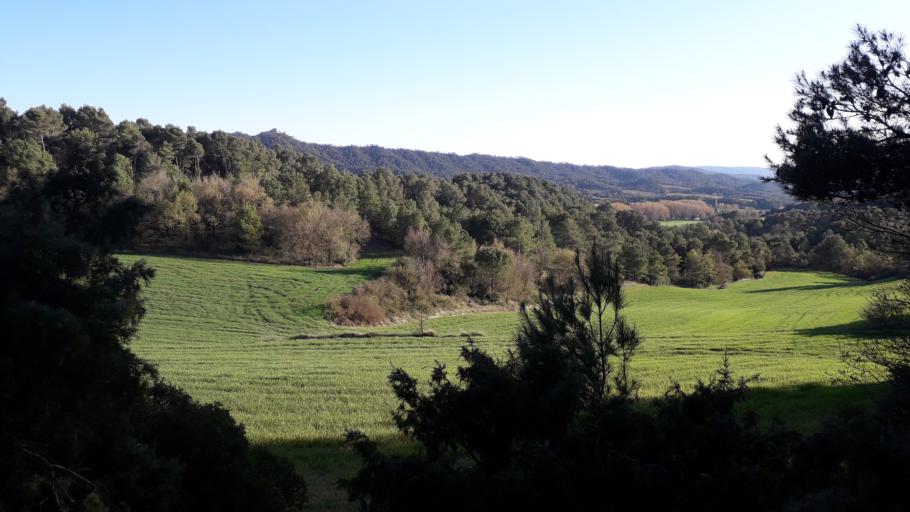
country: ES
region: Catalonia
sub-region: Provincia de Barcelona
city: Bellprat
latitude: 41.5350
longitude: 1.4587
